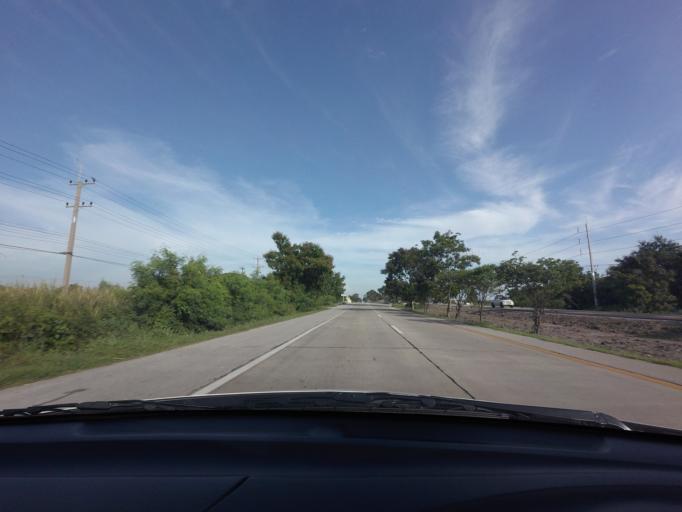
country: TH
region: Phra Nakhon Si Ayutthaya
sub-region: Amphoe Bang Sai
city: Bang Sai
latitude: 14.2524
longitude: 100.2614
